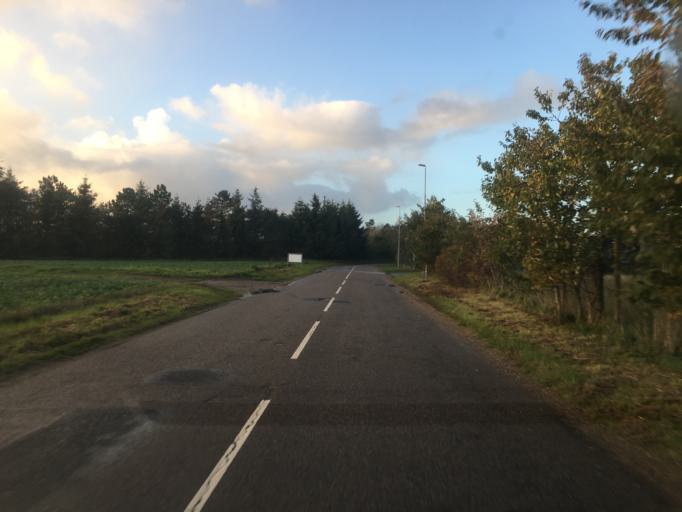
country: DK
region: South Denmark
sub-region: Tonder Kommune
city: Tonder
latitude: 54.9256
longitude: 8.8506
